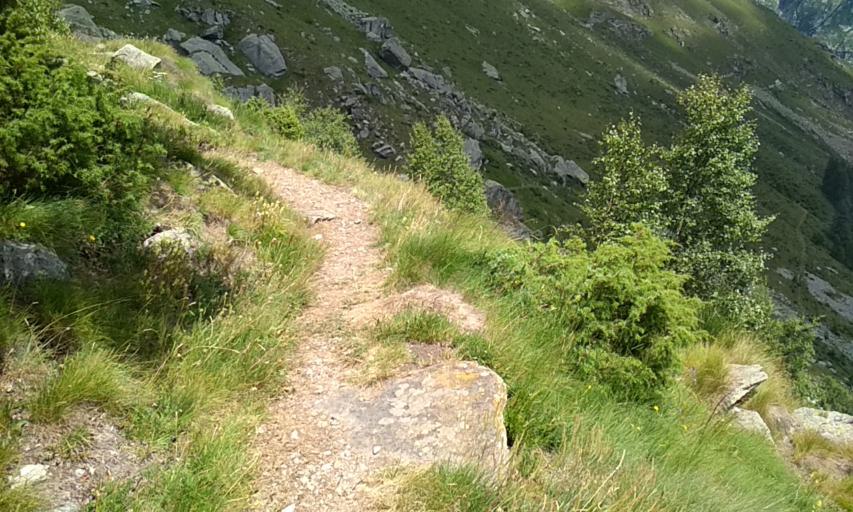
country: IT
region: Piedmont
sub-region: Provincia di Torino
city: Noasca
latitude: 45.4659
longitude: 7.2979
